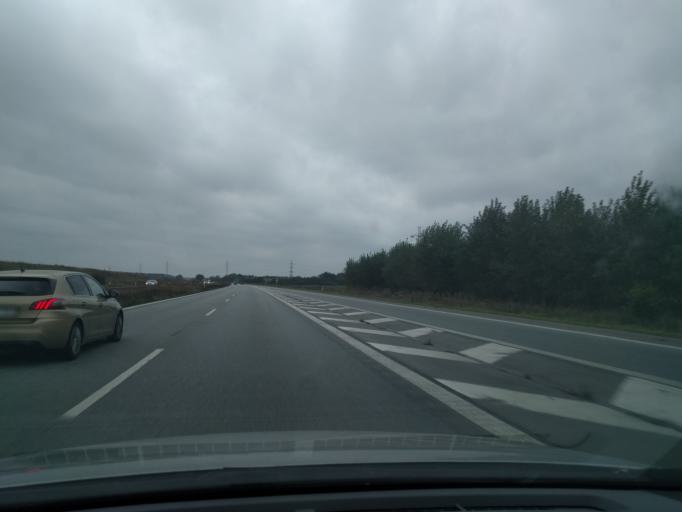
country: DK
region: Zealand
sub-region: Koge Kommune
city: Borup
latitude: 55.4585
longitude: 11.9873
